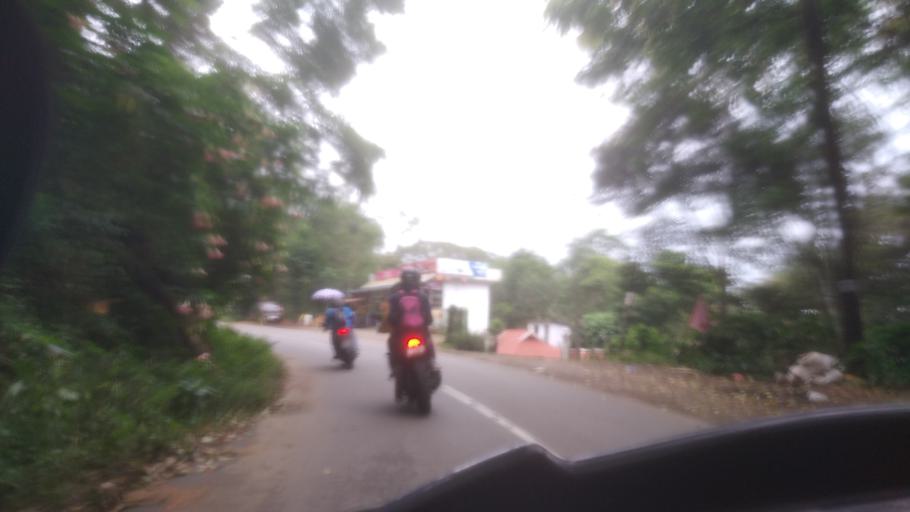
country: IN
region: Tamil Nadu
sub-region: Theni
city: Kombai
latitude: 9.8939
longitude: 77.1583
